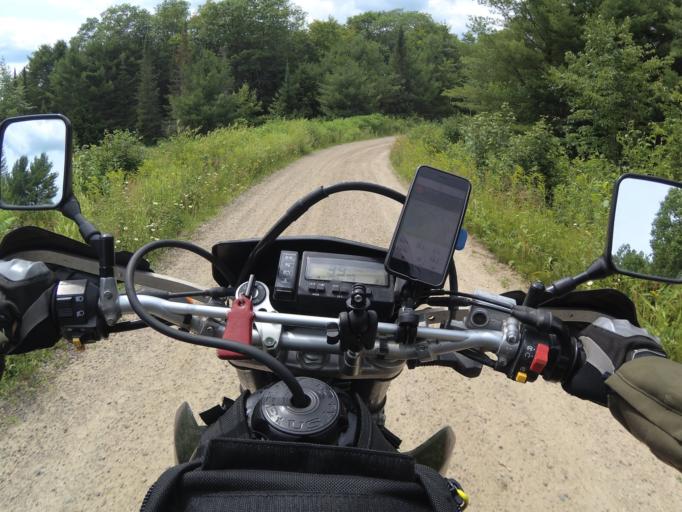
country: CA
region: Ontario
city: Bancroft
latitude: 44.8278
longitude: -77.3077
